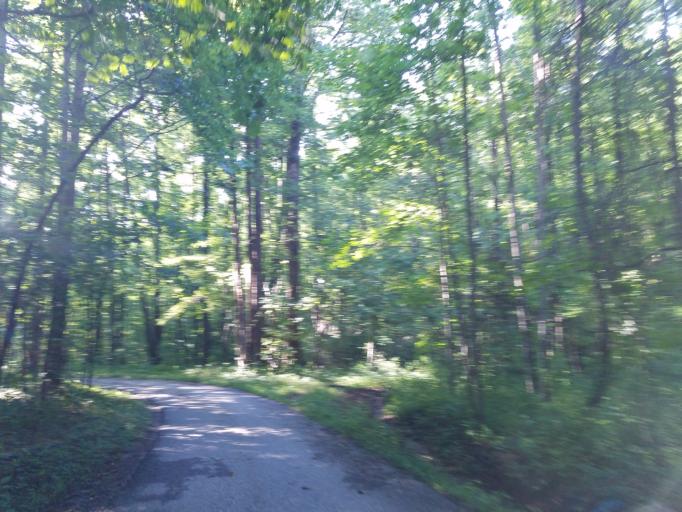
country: US
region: Georgia
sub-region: Lumpkin County
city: Dahlonega
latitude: 34.6748
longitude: -84.0124
